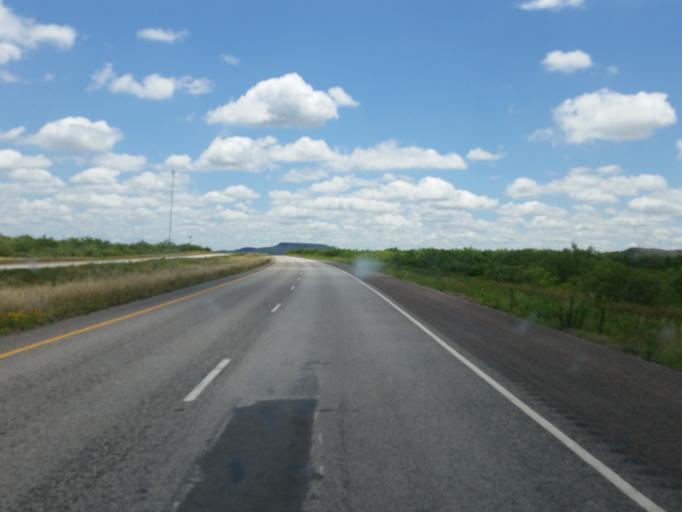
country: US
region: Texas
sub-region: Garza County
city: Post
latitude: 32.9877
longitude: -101.1362
